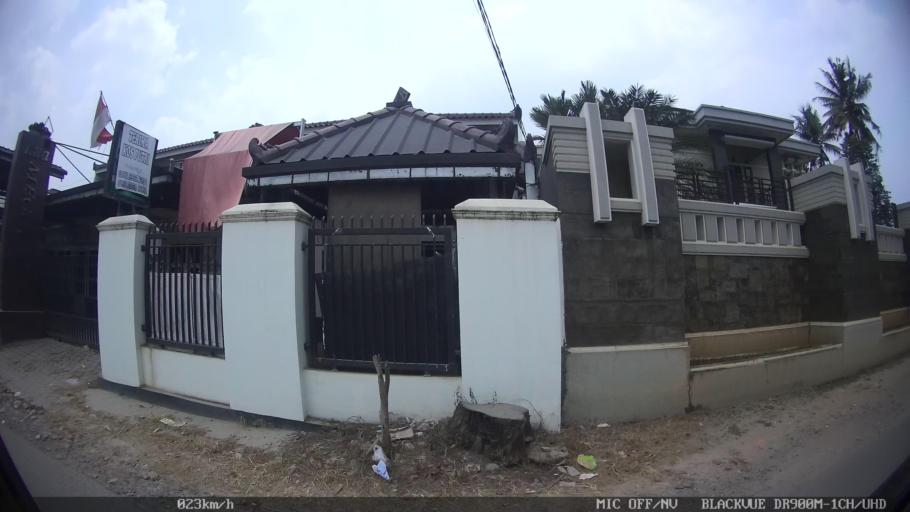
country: ID
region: Lampung
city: Kedaton
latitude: -5.3964
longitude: 105.3038
